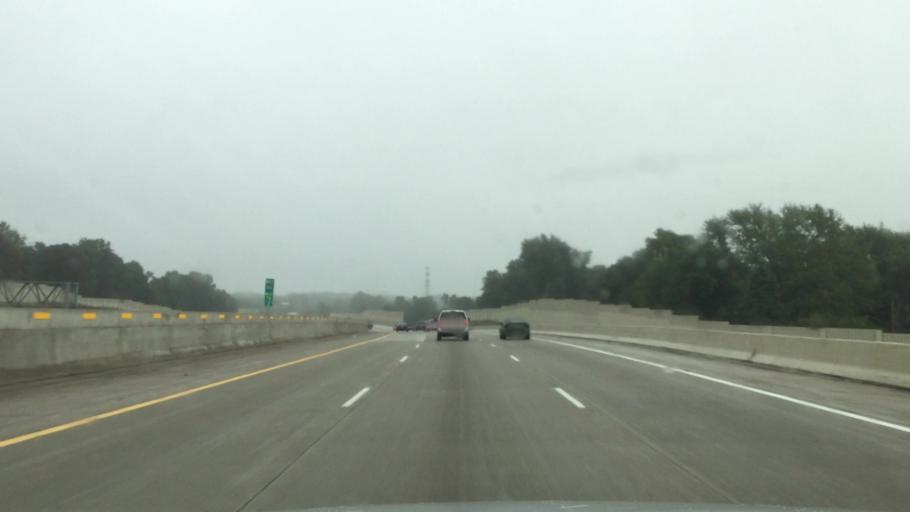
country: US
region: Michigan
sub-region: Kalamazoo County
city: Portage
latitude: 42.2367
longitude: -85.5884
